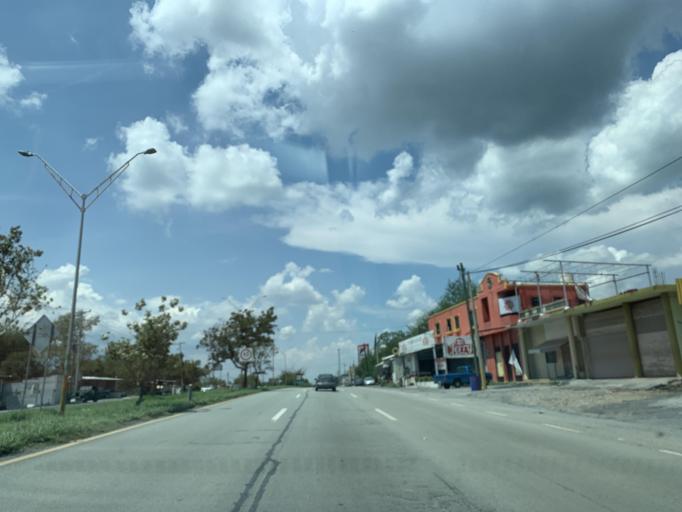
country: MX
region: Nuevo Leon
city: Santiago
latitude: 25.3828
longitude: -100.1140
